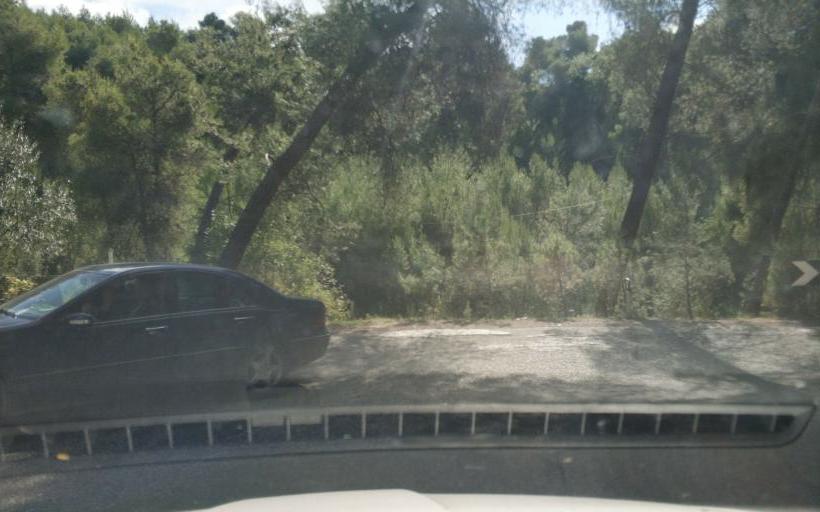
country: AL
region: Durres
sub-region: Rrethi i Krujes
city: Kruje
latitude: 41.4910
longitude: 19.7696
